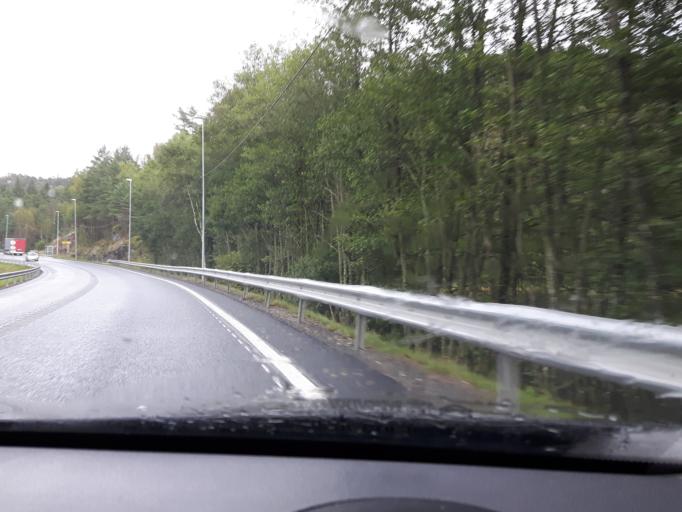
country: NO
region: Vest-Agder
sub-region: Marnardal
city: Helland
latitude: 58.0916
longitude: 7.6276
